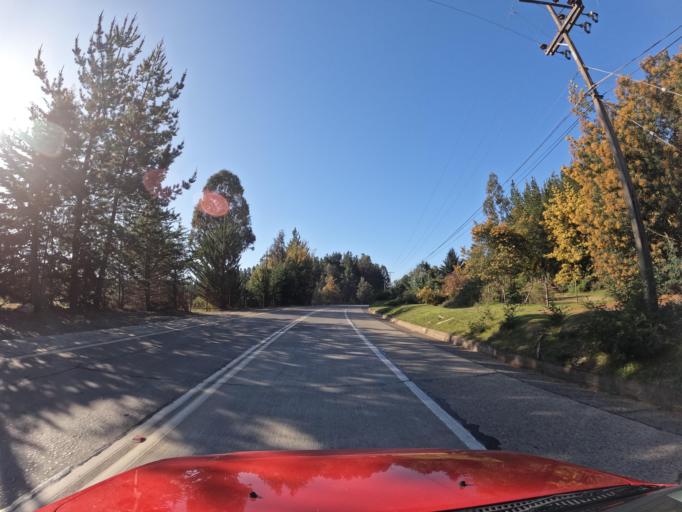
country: CL
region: Maule
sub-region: Provincia de Talca
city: Constitucion
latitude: -35.4326
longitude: -72.3353
